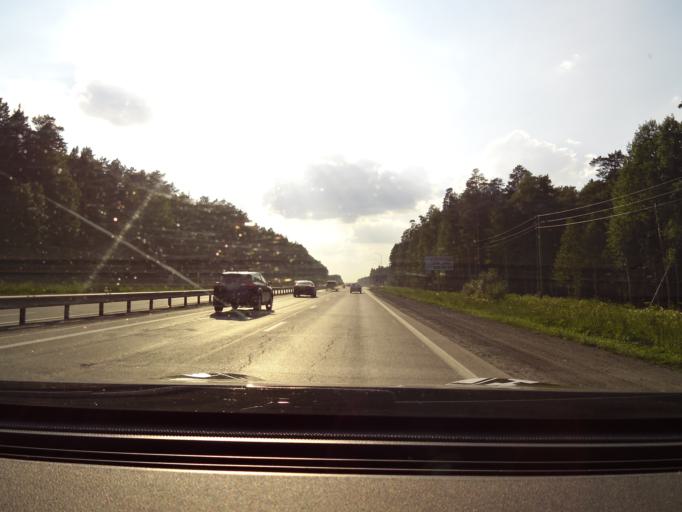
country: RU
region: Sverdlovsk
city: Severka
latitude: 56.8378
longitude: 60.2760
